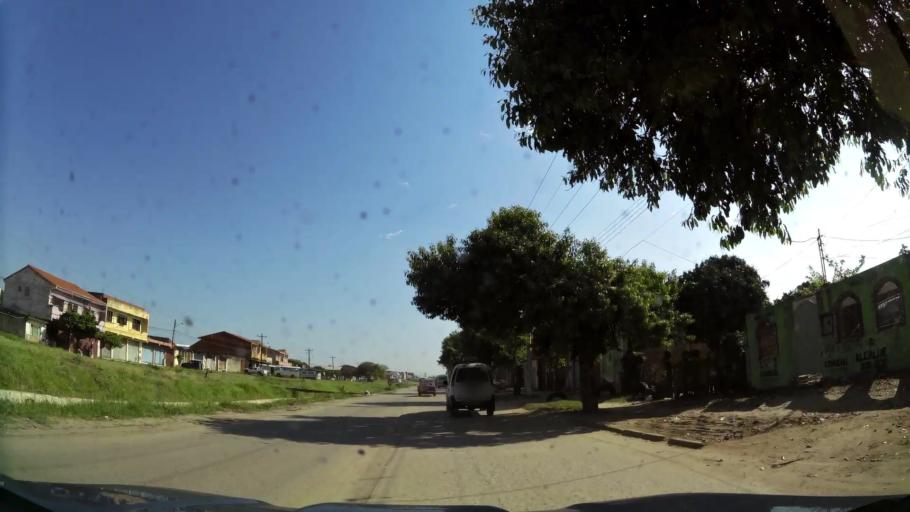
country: BO
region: Santa Cruz
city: Santa Cruz de la Sierra
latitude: -17.8218
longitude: -63.1255
